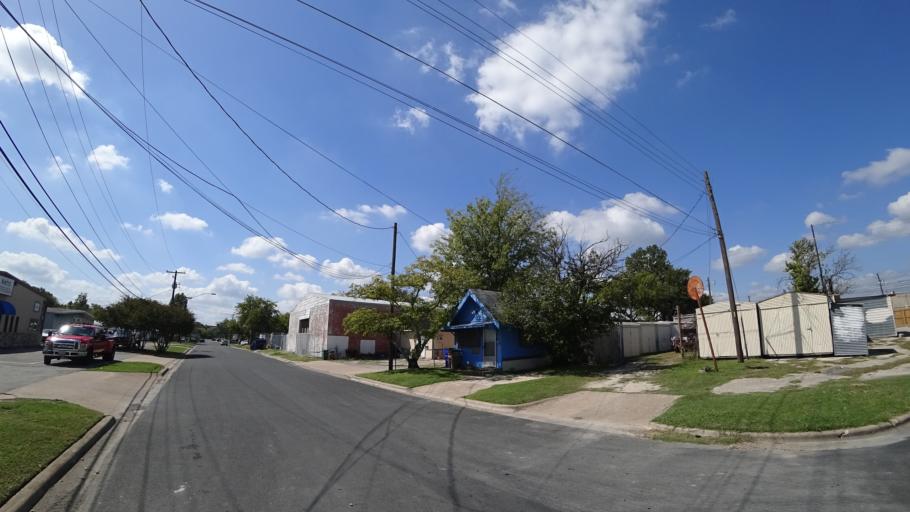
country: US
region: Texas
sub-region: Travis County
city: Austin
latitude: 30.3347
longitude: -97.7195
